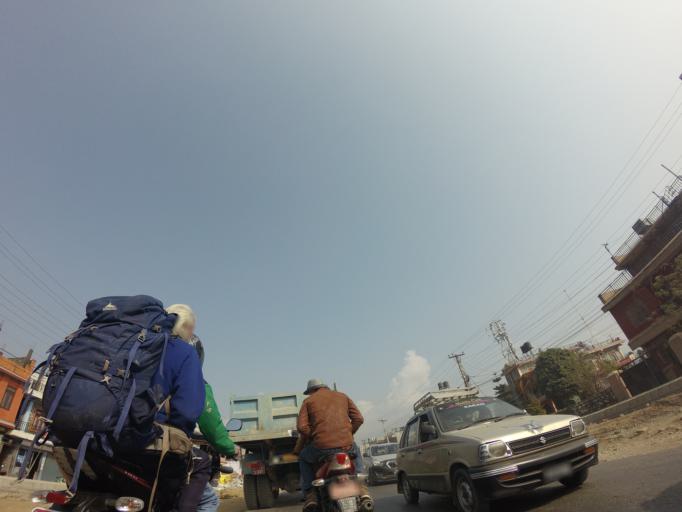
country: NP
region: Western Region
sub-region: Gandaki Zone
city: Pokhara
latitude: 28.2202
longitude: 83.9778
